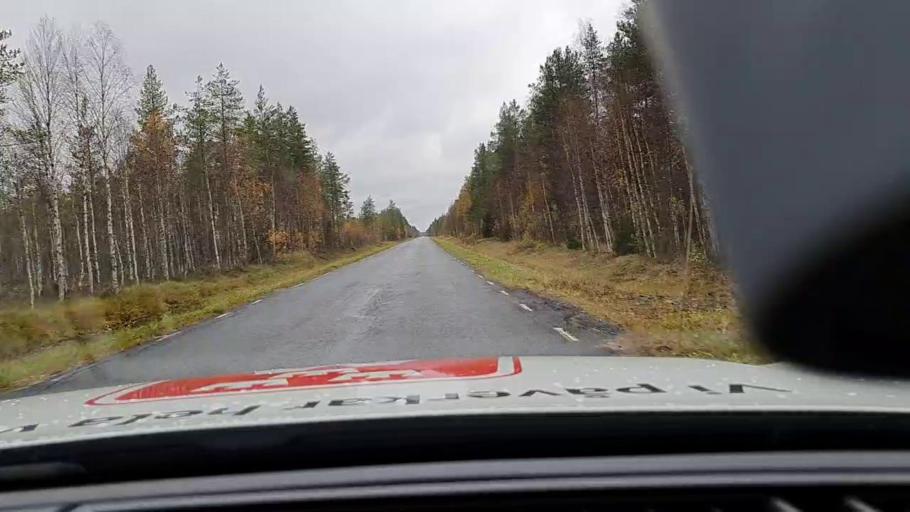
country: SE
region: Norrbotten
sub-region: Haparanda Kommun
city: Haparanda
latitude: 65.9062
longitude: 23.8324
